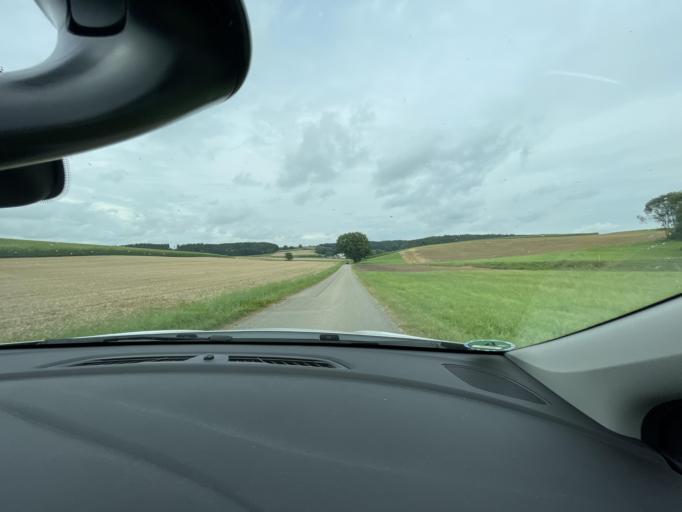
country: DE
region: Bavaria
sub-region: Swabia
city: Aindling
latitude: 48.5642
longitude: 10.9724
